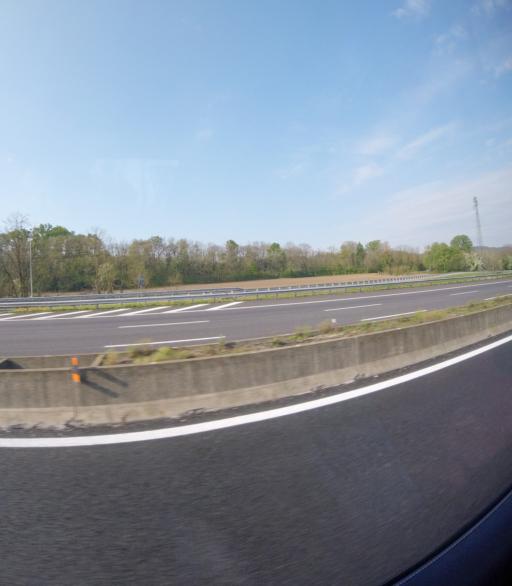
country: IT
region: Piedmont
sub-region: Provincia di Novara
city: Borgo Ticino
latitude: 45.7003
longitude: 8.6094
